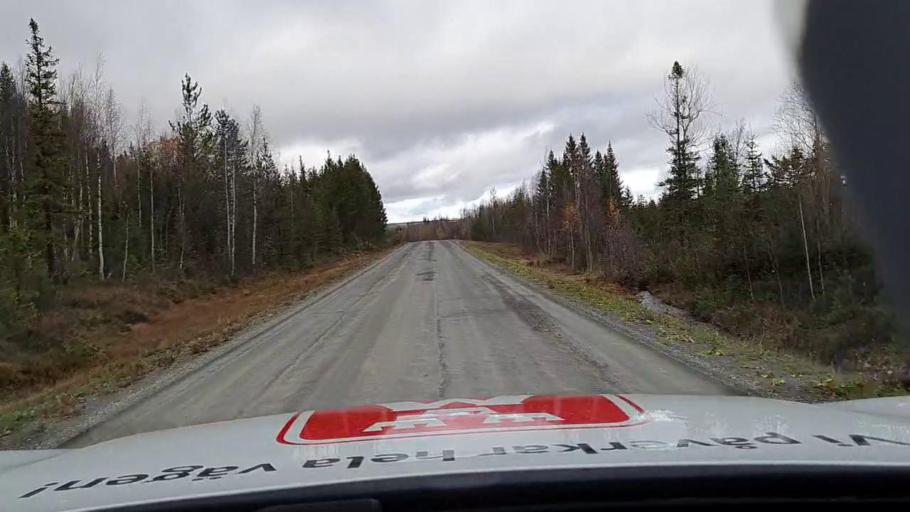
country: SE
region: Jaemtland
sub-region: Krokoms Kommun
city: Valla
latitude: 63.0548
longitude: 13.9634
